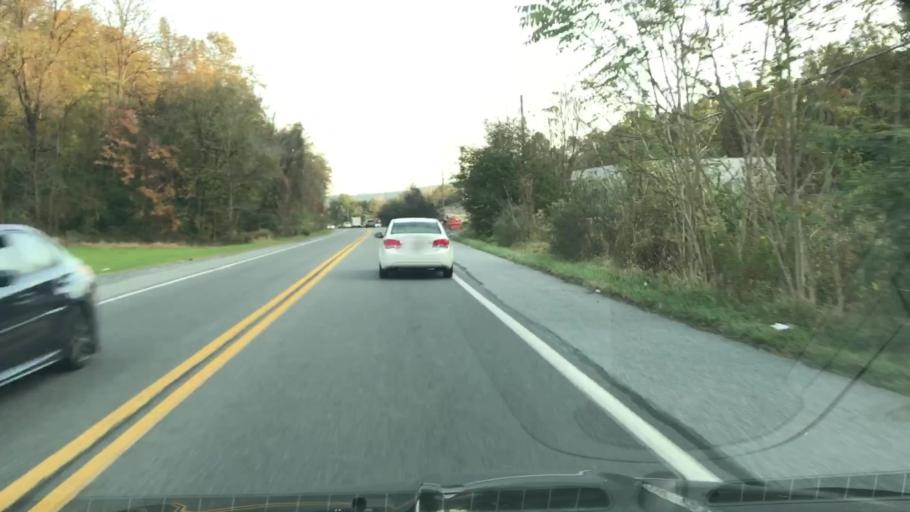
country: US
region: Pennsylvania
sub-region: Dauphin County
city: Bressler
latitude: 40.2308
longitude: -76.8006
